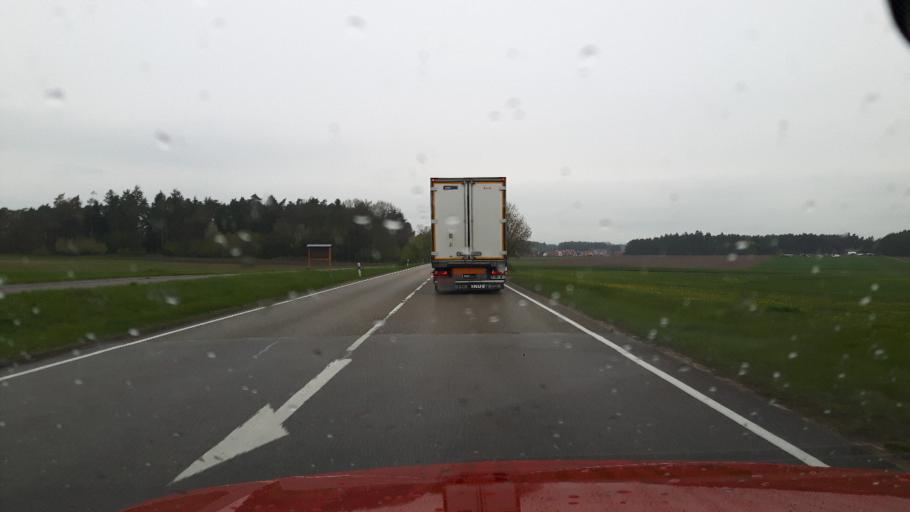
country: DE
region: Bavaria
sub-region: Regierungsbezirk Mittelfranken
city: Weidenbach
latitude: 49.2223
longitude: 10.6336
